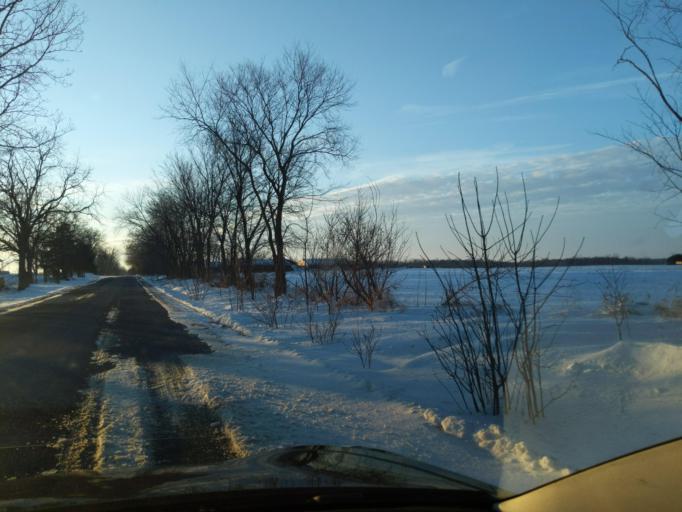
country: US
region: Michigan
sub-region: Ingham County
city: Webberville
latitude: 42.5698
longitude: -84.1979
